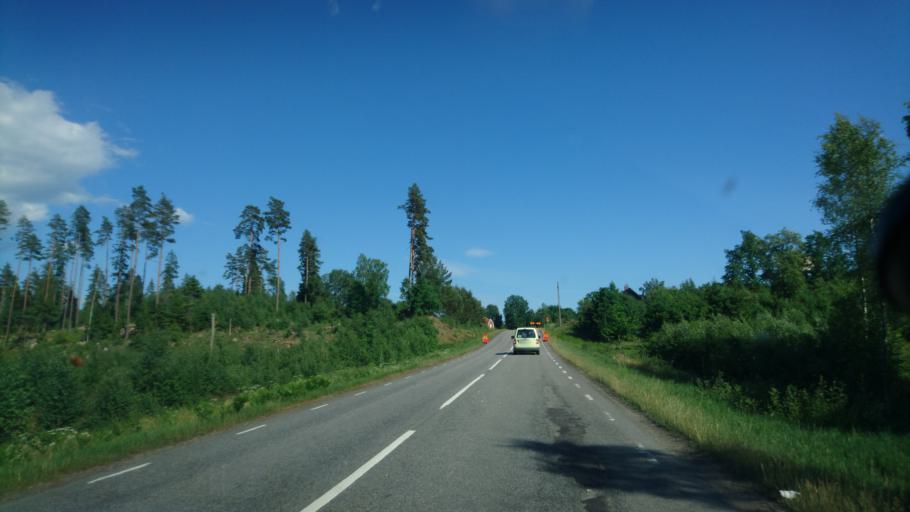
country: SE
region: Skane
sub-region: Osby Kommun
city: Lonsboda
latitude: 56.4084
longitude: 14.3131
